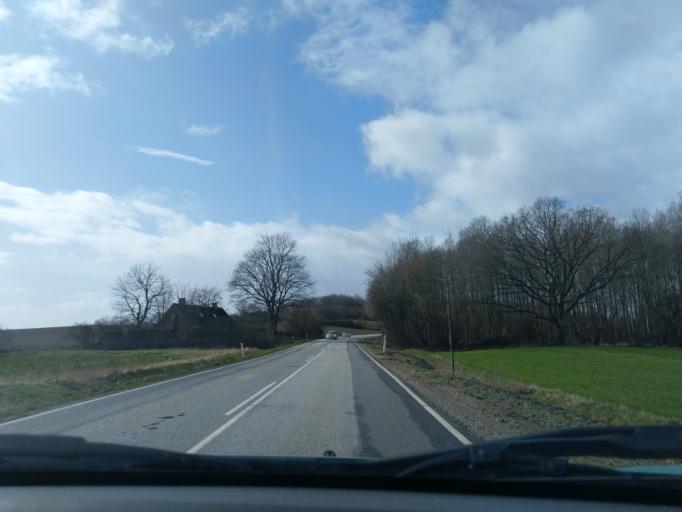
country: DK
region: Zealand
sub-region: Naestved Kommune
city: Fuglebjerg
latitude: 55.3216
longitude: 11.6212
